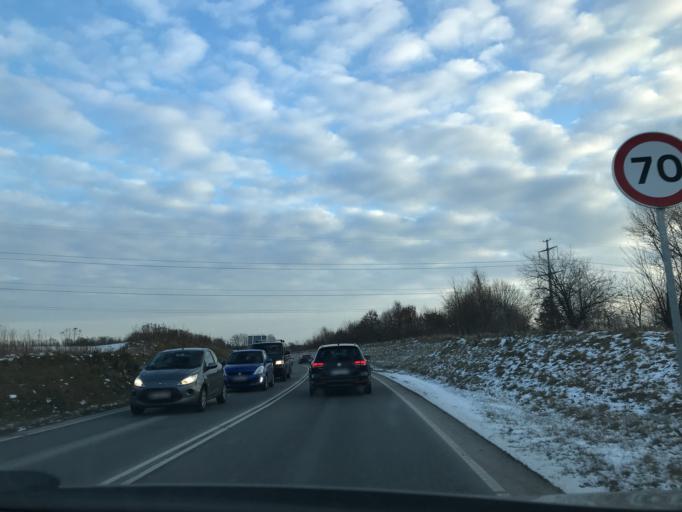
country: DK
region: Capital Region
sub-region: Egedal Kommune
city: Smorumnedre
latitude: 55.7288
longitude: 12.3100
